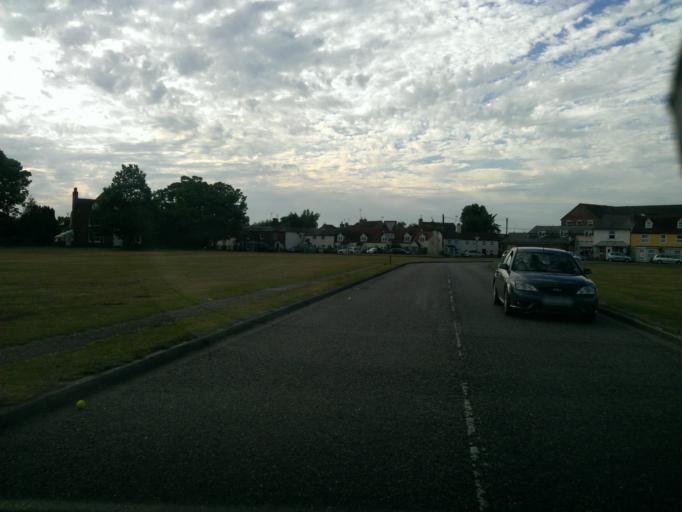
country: GB
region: England
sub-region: Essex
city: Great Bentley
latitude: 51.8539
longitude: 1.0635
